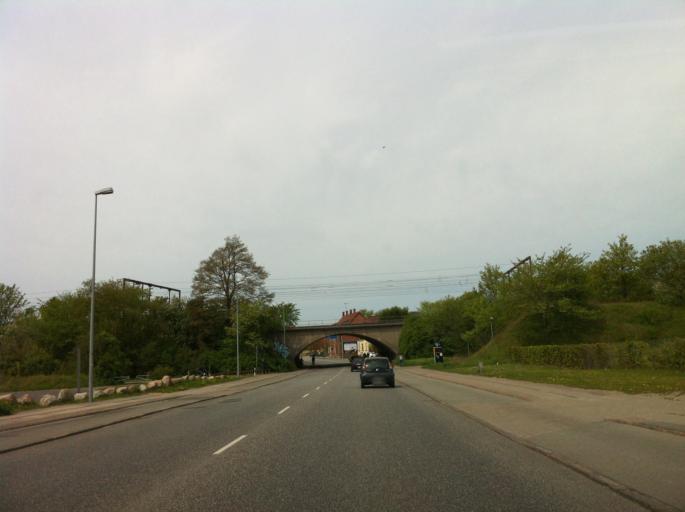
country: DK
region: Zealand
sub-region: Roskilde Kommune
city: Roskilde
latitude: 55.6323
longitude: 12.0776
